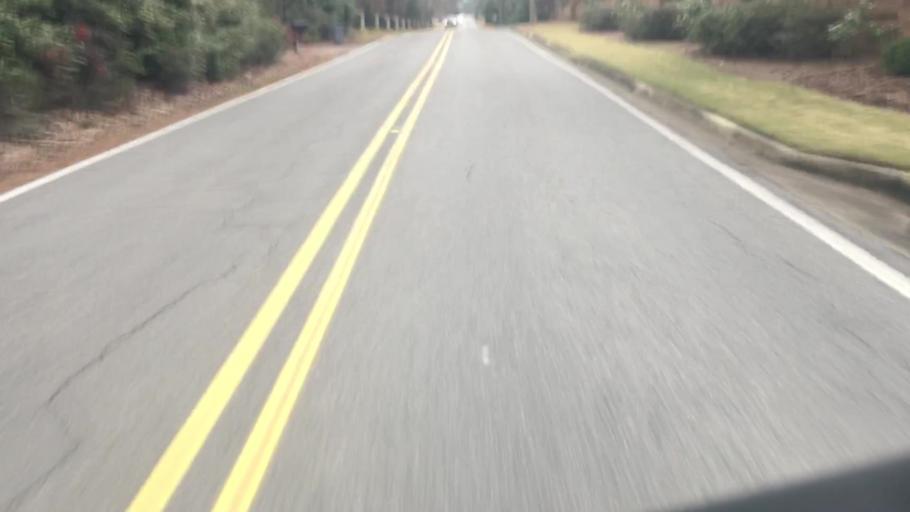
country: US
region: Alabama
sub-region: Jefferson County
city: Vestavia Hills
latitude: 33.4208
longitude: -86.7590
